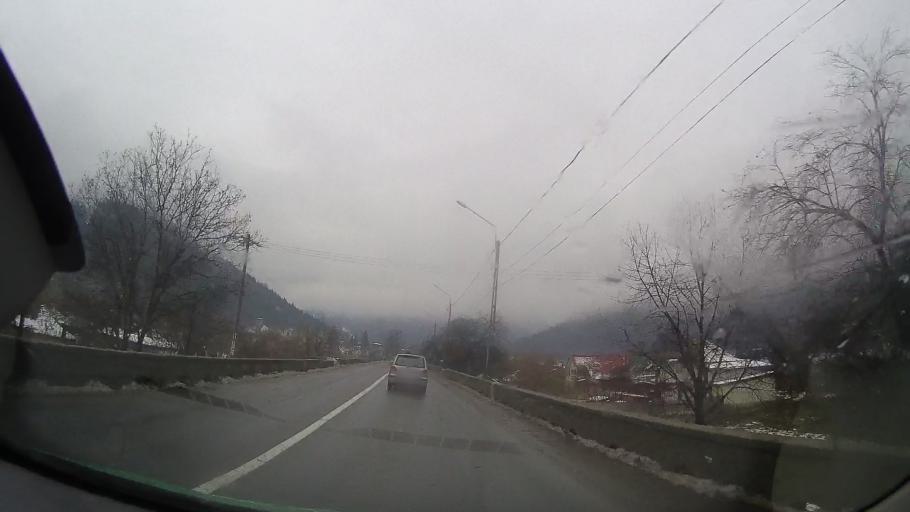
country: RO
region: Neamt
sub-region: Comuna Bicaz
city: Dodeni
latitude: 46.9064
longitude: 26.1072
